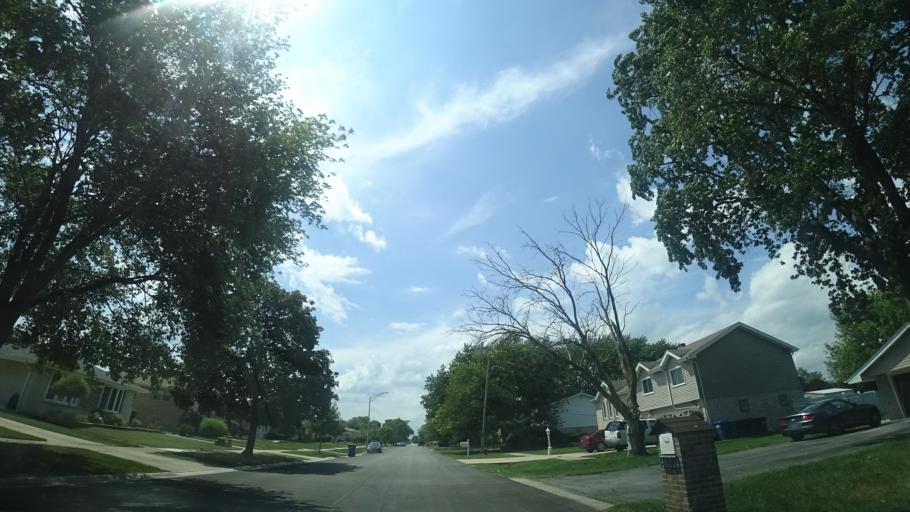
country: US
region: Illinois
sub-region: Cook County
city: Alsip
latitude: 41.6735
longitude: -87.7443
